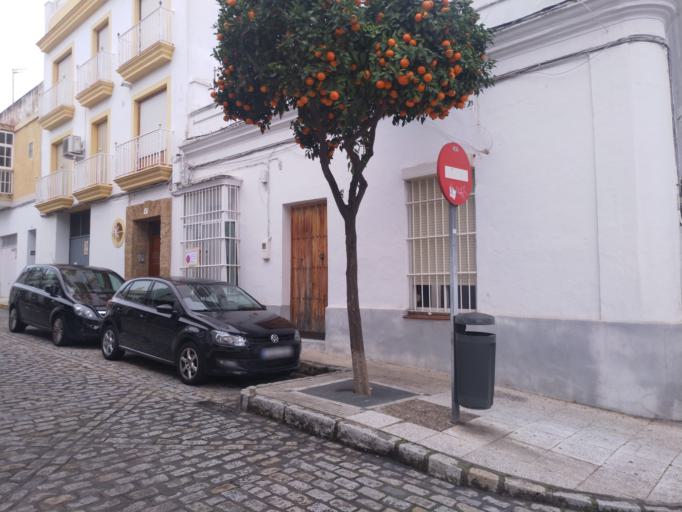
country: ES
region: Andalusia
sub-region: Provincia de Cadiz
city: San Fernando
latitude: 36.4725
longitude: -6.1951
